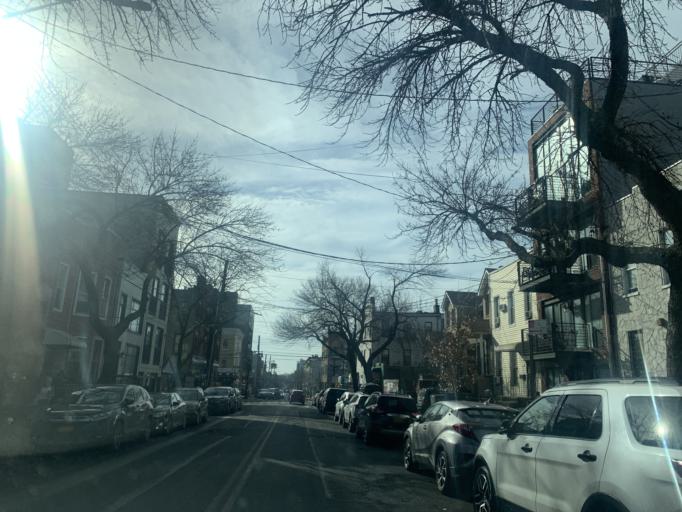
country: US
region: New York
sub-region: Queens County
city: Long Island City
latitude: 40.7050
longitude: -73.9186
